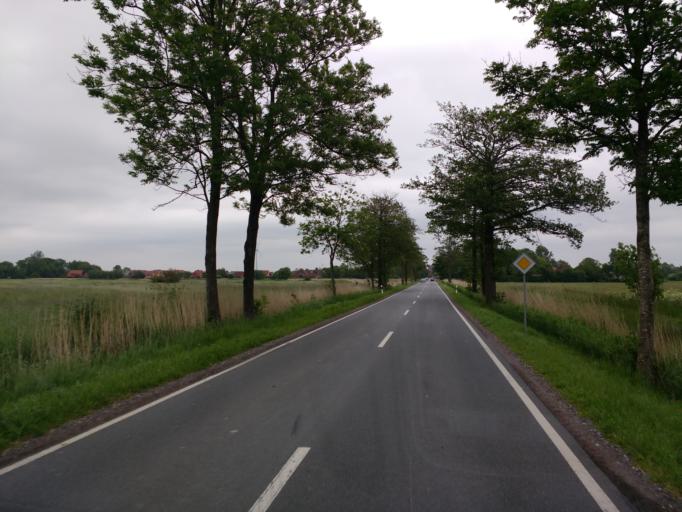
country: DE
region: Lower Saxony
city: Sillenstede
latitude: 53.6105
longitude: 7.9437
